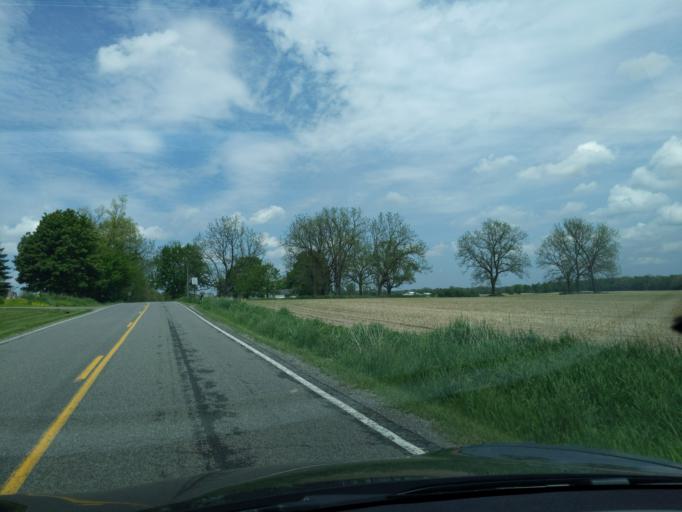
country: US
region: Michigan
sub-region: Ingham County
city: Stockbridge
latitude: 42.4911
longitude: -84.1602
